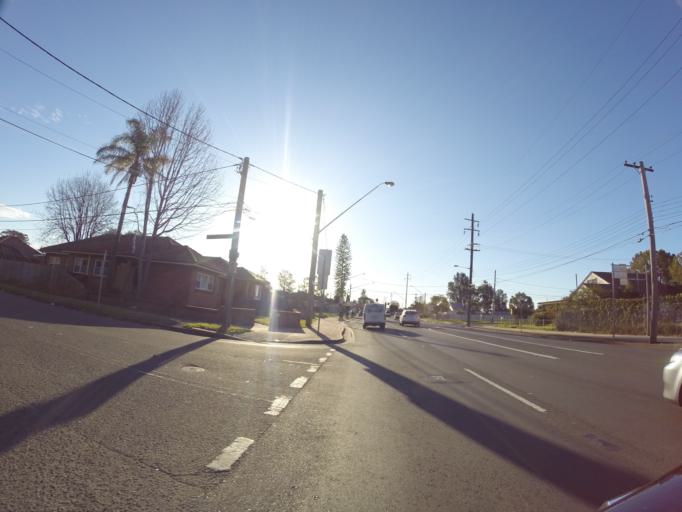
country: AU
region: New South Wales
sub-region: Fairfield
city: Fairfield Heights
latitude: -33.8651
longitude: 150.9550
